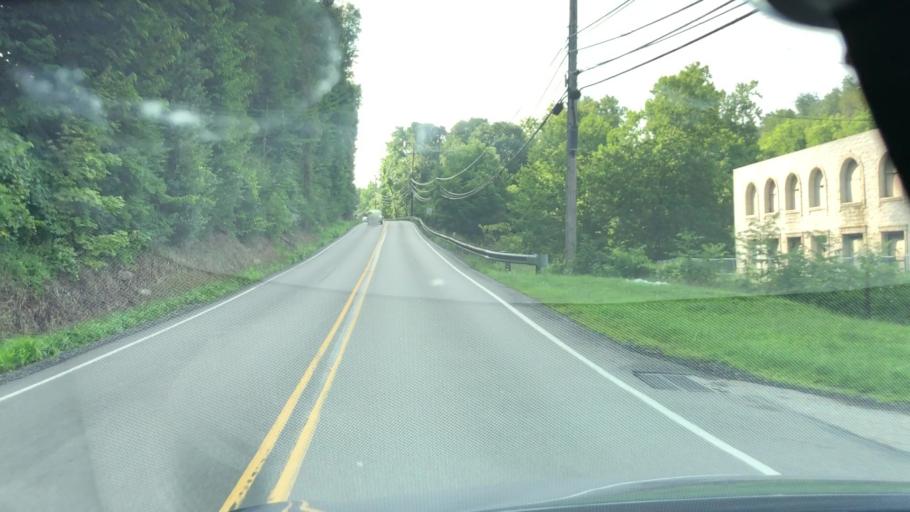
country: US
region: Pennsylvania
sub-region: Washington County
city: Thompsonville
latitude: 40.2892
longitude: -80.1033
